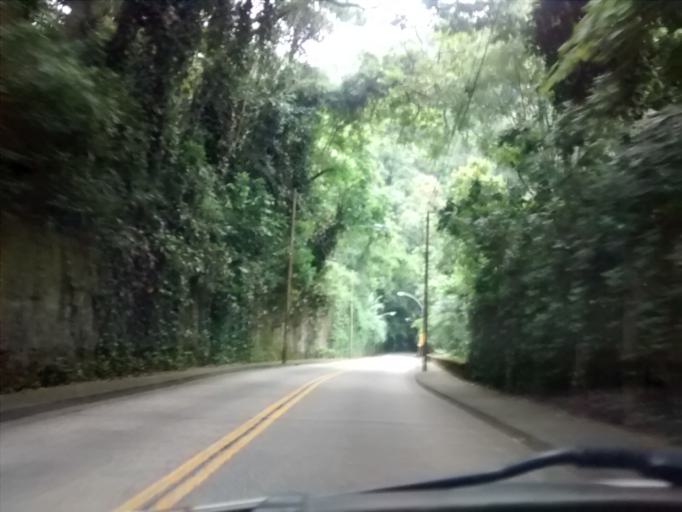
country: BR
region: Rio de Janeiro
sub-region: Rio De Janeiro
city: Rio de Janeiro
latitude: -22.9835
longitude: -43.2742
